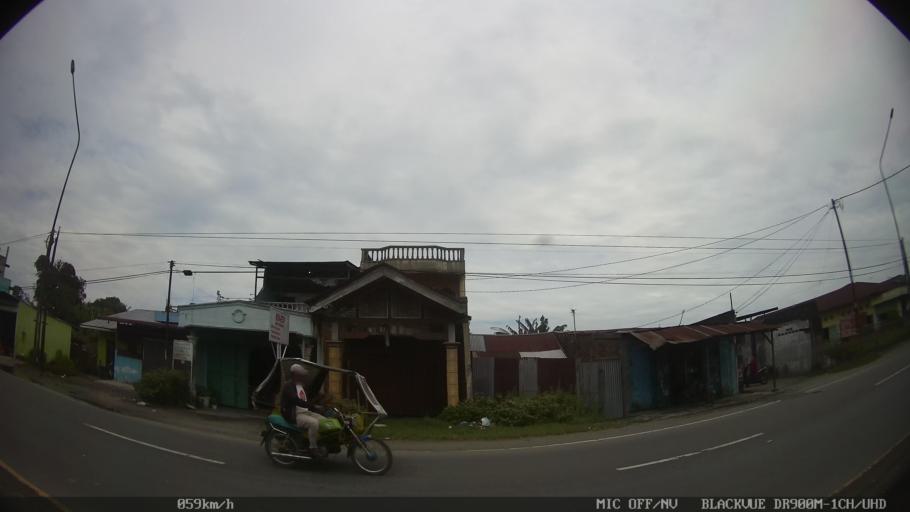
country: ID
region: North Sumatra
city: Sunggal
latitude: 3.5996
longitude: 98.5692
